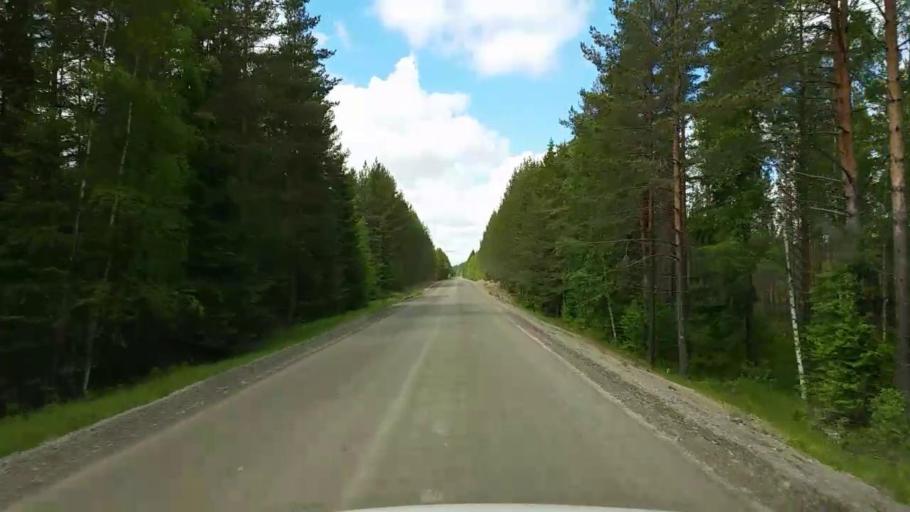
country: SE
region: Gaevleborg
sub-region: Bollnas Kommun
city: Vittsjo
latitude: 61.0337
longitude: 16.3674
